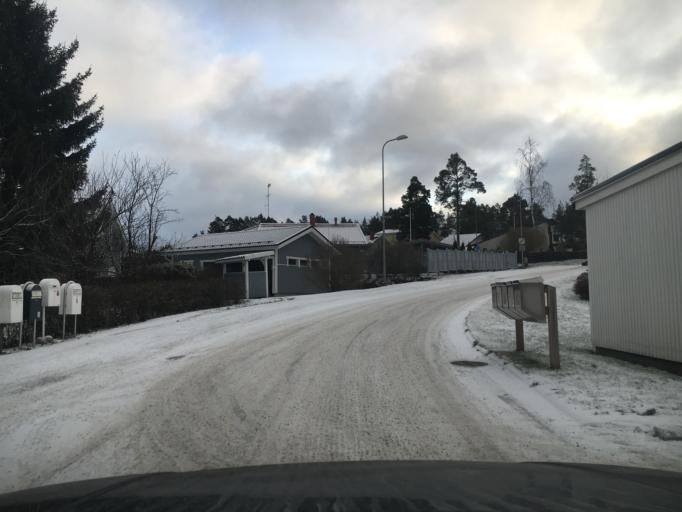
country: FI
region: Uusimaa
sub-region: Helsinki
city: Espoo
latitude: 60.1634
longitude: 24.6620
